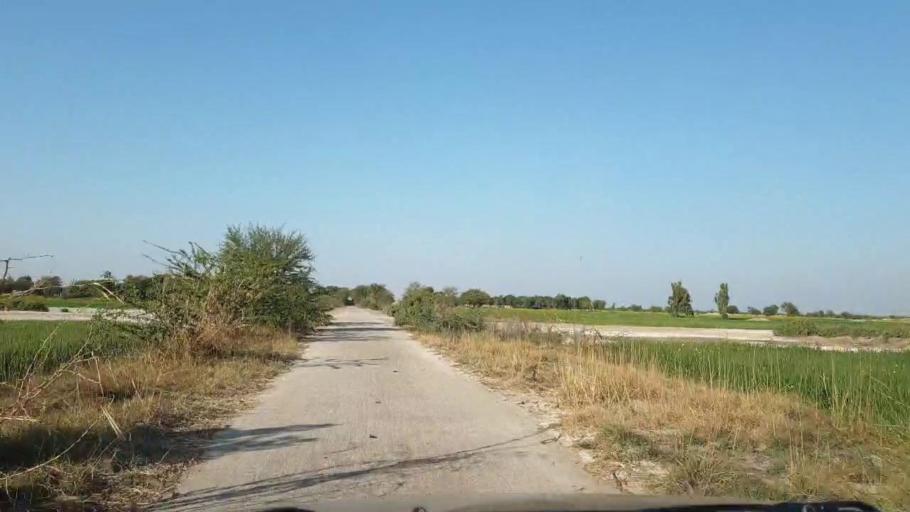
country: PK
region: Sindh
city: Khadro
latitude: 26.2118
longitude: 68.7542
